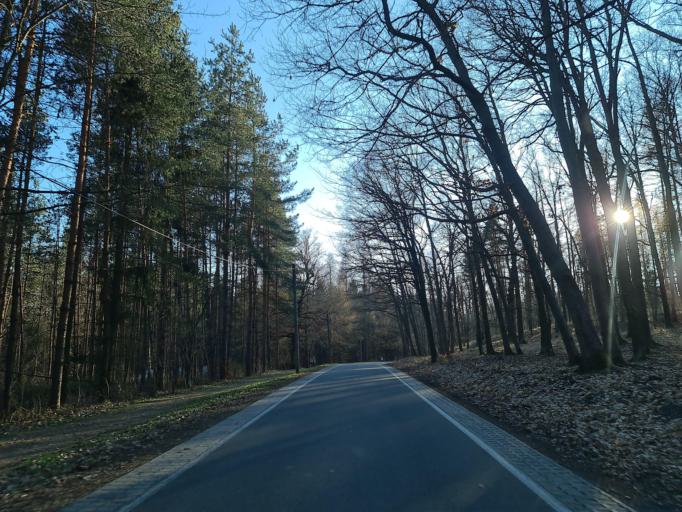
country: DE
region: Saxony
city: Pohl
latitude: 50.5317
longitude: 12.1566
